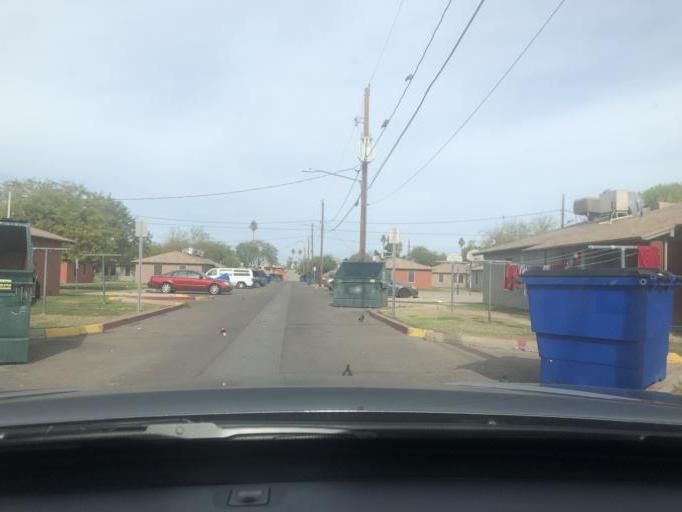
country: US
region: Arizona
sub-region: Maricopa County
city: Phoenix
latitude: 33.4544
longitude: -112.0399
